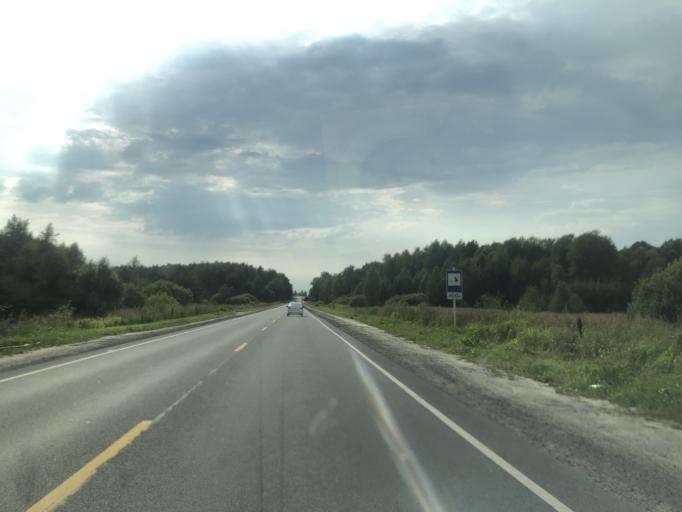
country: RU
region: Ivanovo
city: Shuya
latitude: 56.8585
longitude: 41.4915
